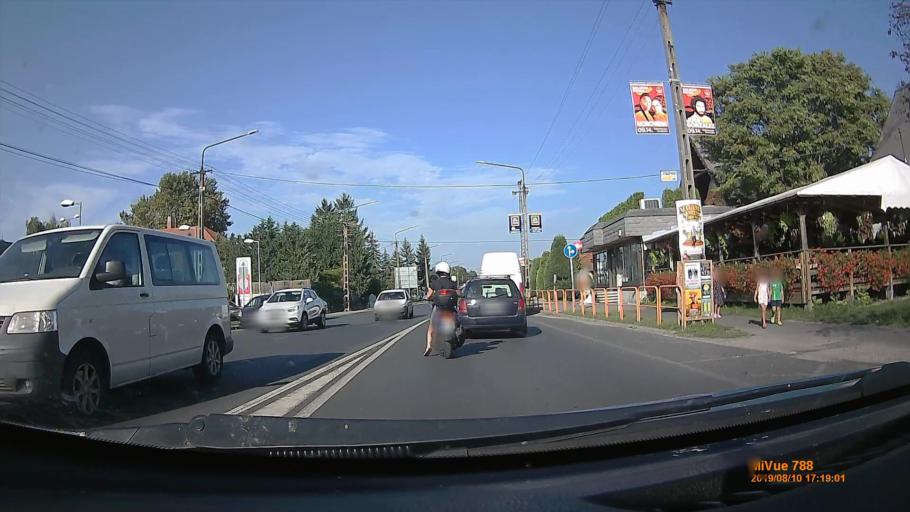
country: HU
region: Somogy
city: Balatonlelle
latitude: 46.7874
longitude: 17.6980
